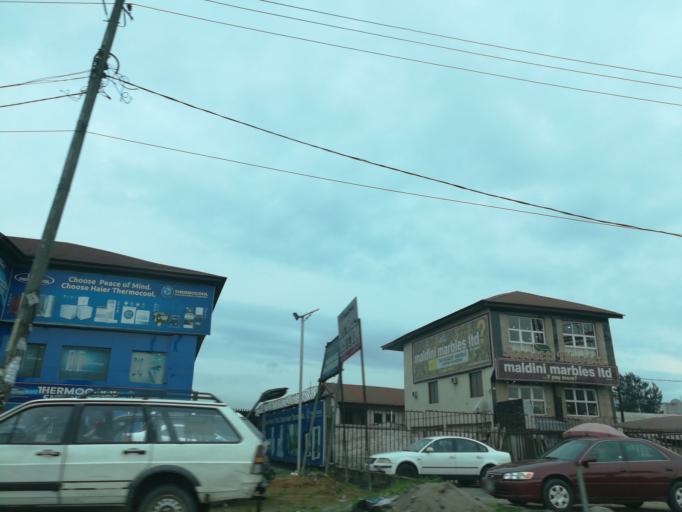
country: NG
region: Rivers
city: Port Harcourt
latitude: 4.8361
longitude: 7.0182
